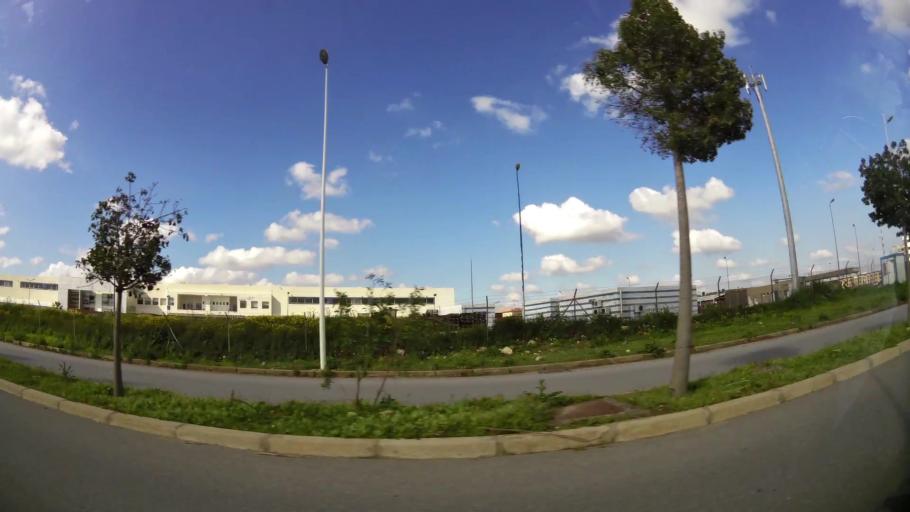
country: MA
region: Grand Casablanca
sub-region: Mediouna
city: Mediouna
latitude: 33.3884
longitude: -7.5381
